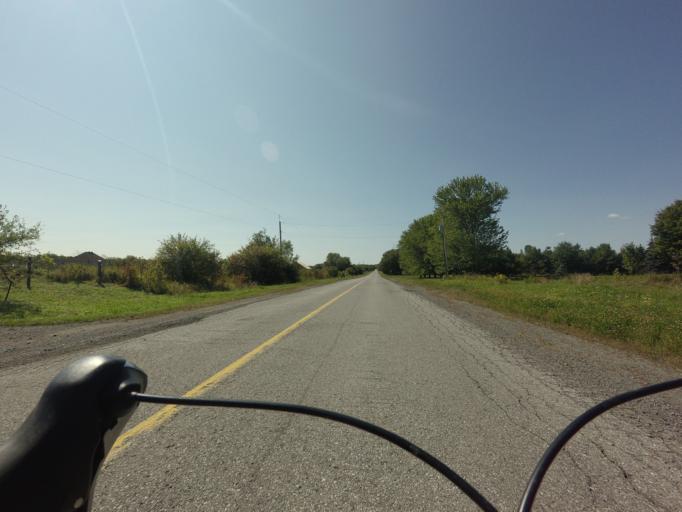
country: CA
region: Ontario
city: Bells Corners
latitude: 45.3850
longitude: -76.0025
